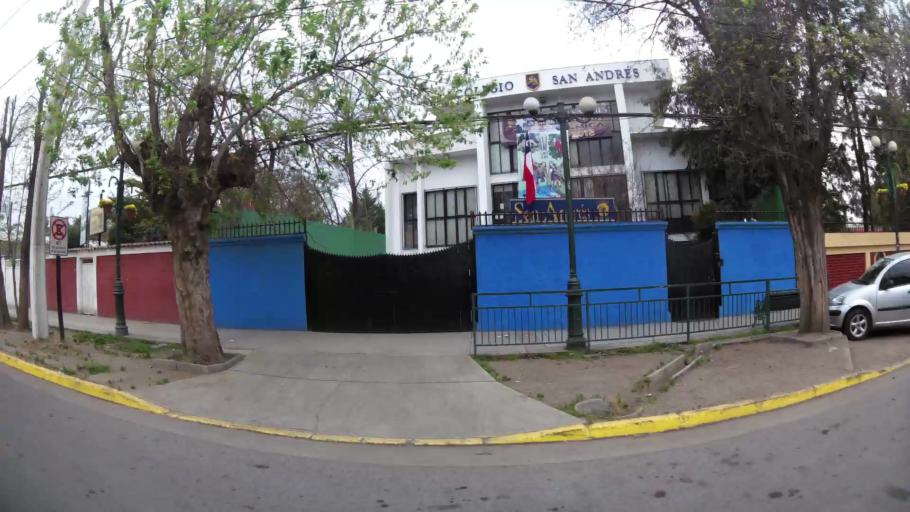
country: CL
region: Santiago Metropolitan
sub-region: Provincia de Chacabuco
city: Chicureo Abajo
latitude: -33.2039
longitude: -70.6808
